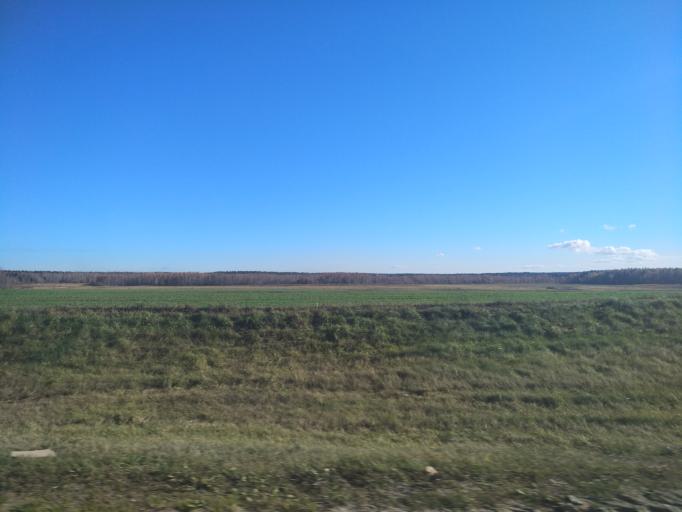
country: BY
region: Minsk
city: Il'ya
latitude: 54.5507
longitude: 27.2119
